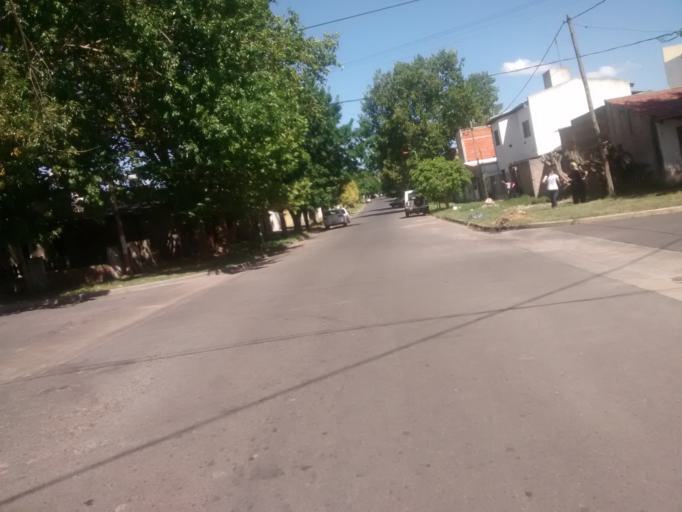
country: AR
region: Buenos Aires
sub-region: Partido de La Plata
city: La Plata
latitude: -34.9330
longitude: -57.9277
